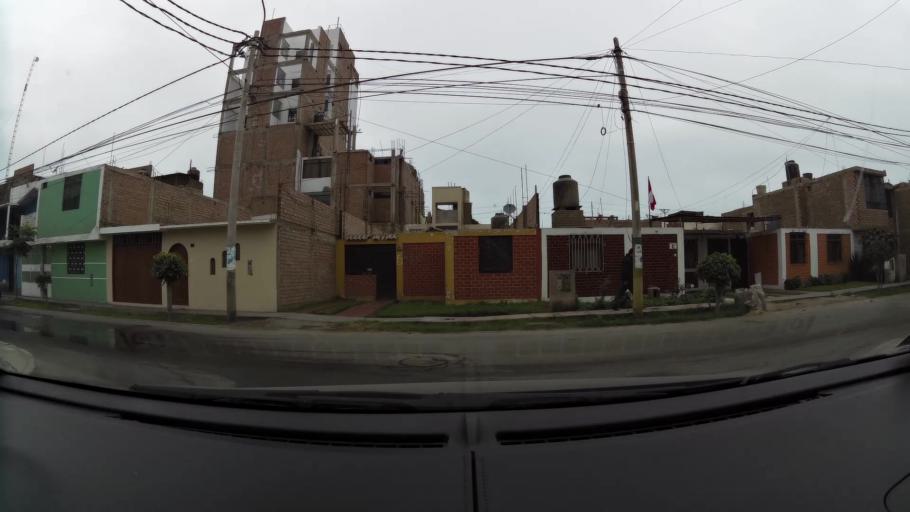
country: PE
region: Lima
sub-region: Barranca
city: Barranca
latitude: -10.7439
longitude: -77.7660
